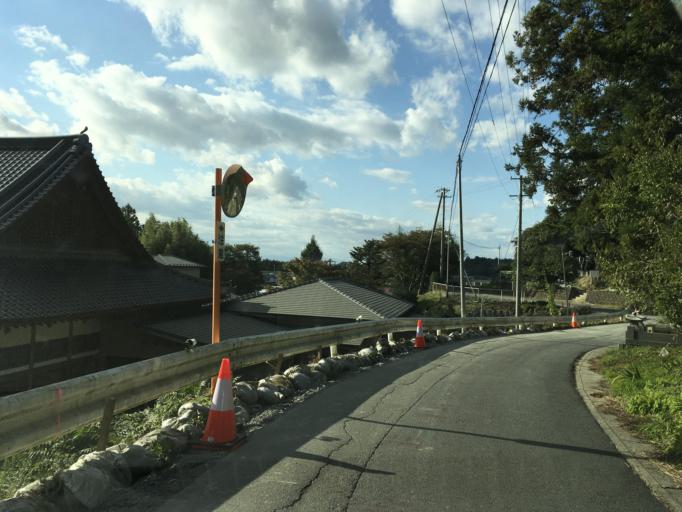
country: JP
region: Miyagi
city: Wakuya
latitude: 38.6500
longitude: 141.2921
